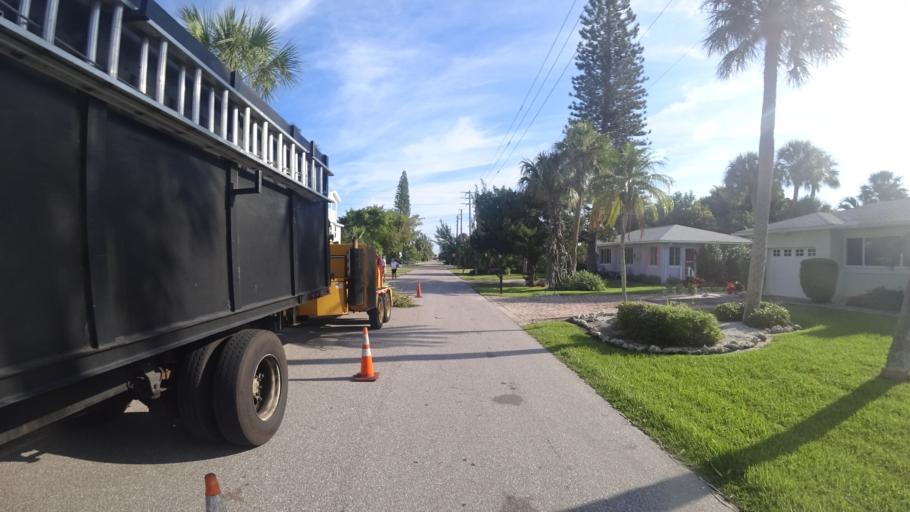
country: US
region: Florida
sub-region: Manatee County
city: Anna Maria
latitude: 27.5189
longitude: -82.7255
